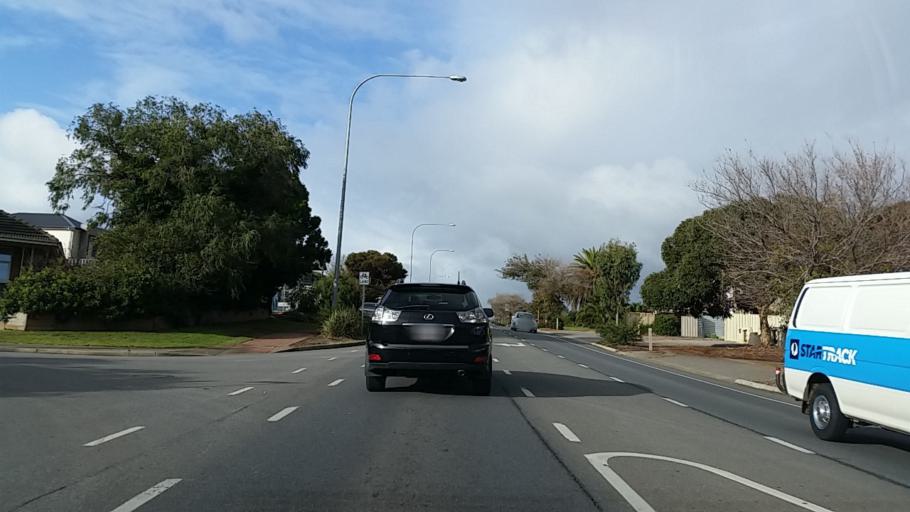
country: AU
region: South Australia
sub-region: Adelaide
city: Port Noarlunga
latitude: -35.1462
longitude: 138.4841
